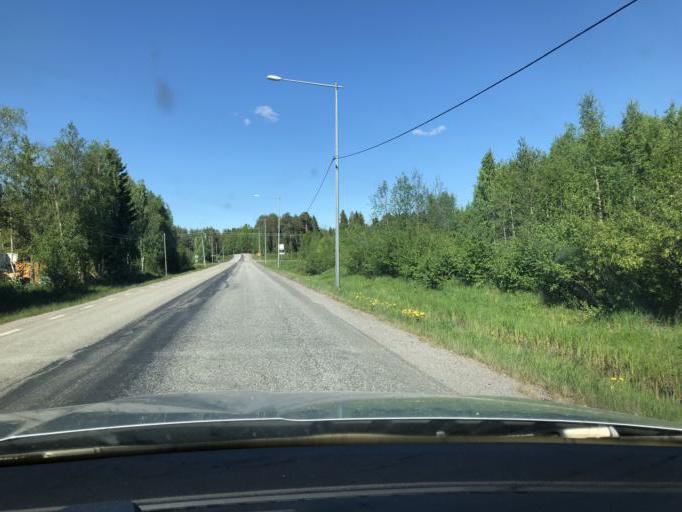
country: SE
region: Norrbotten
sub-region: Kalix Kommun
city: Kalix
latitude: 65.8712
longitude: 23.1496
